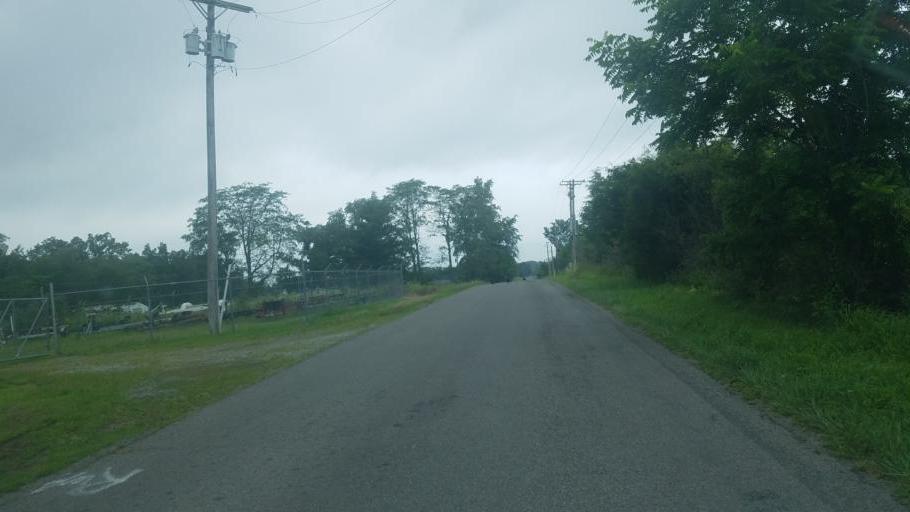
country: US
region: Ohio
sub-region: Logan County
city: Russells Point
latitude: 40.4611
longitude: -83.8571
